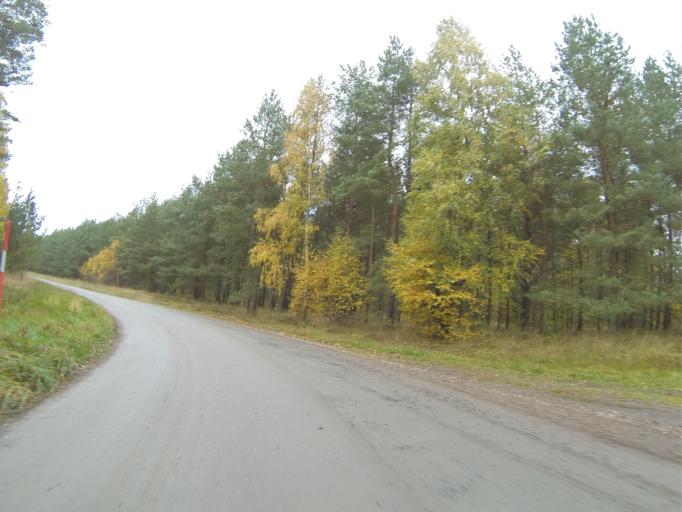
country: SE
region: Skane
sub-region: Sjobo Kommun
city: Sjoebo
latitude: 55.6350
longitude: 13.6436
